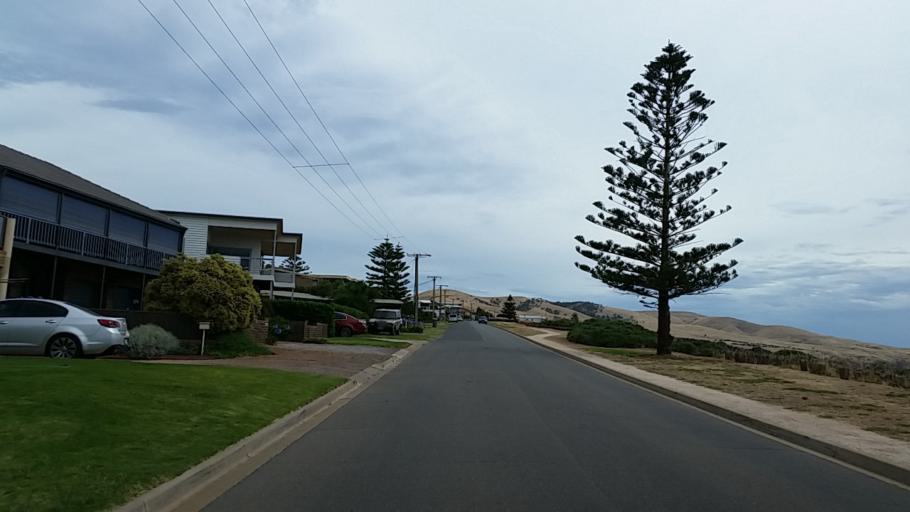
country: AU
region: South Australia
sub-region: Onkaparinga
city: Port Willunga
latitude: -35.3350
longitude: 138.4481
